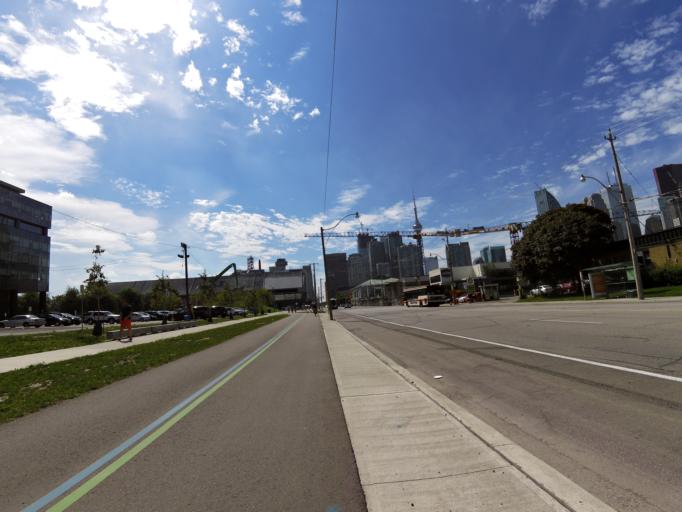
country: CA
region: Ontario
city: Toronto
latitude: 43.6447
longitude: -79.3667
